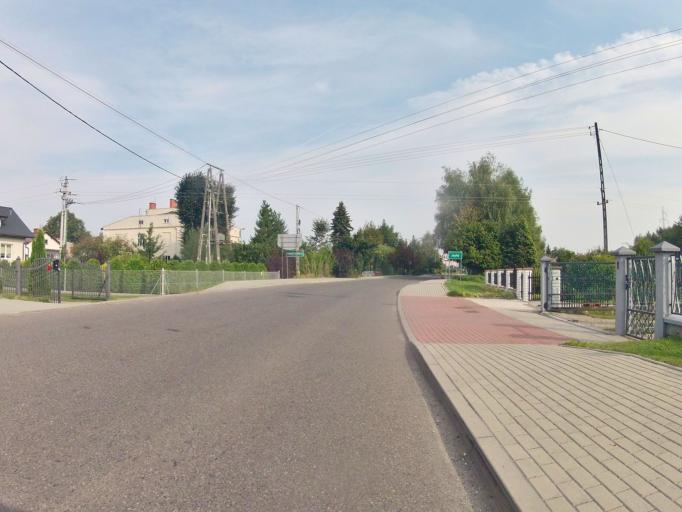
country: PL
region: Subcarpathian Voivodeship
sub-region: Powiat jasielski
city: Debowiec
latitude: 49.7141
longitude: 21.4616
